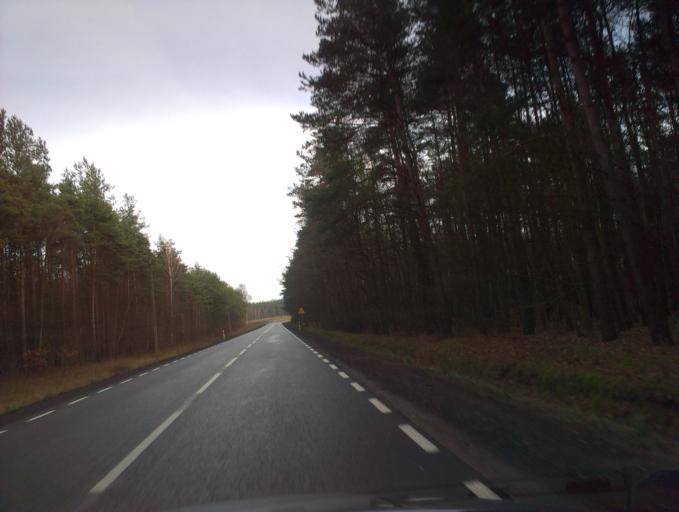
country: PL
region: West Pomeranian Voivodeship
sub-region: Powiat szczecinecki
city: Szczecinek
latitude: 53.7247
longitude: 16.7567
